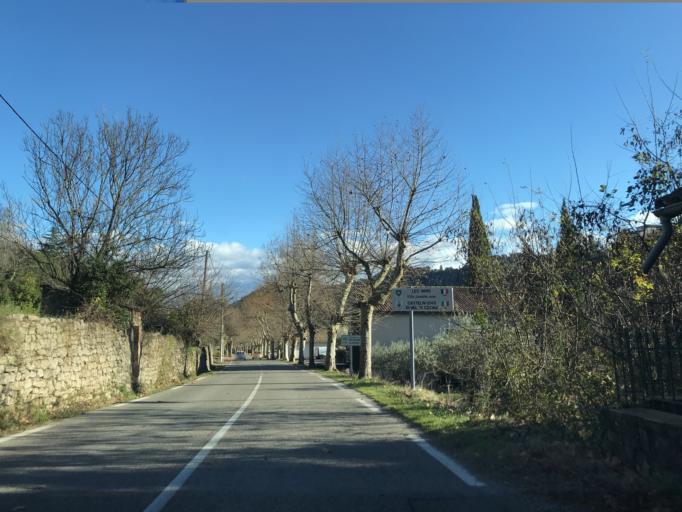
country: FR
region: Rhone-Alpes
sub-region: Departement de l'Ardeche
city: Les Vans
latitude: 44.4066
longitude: 4.1180
